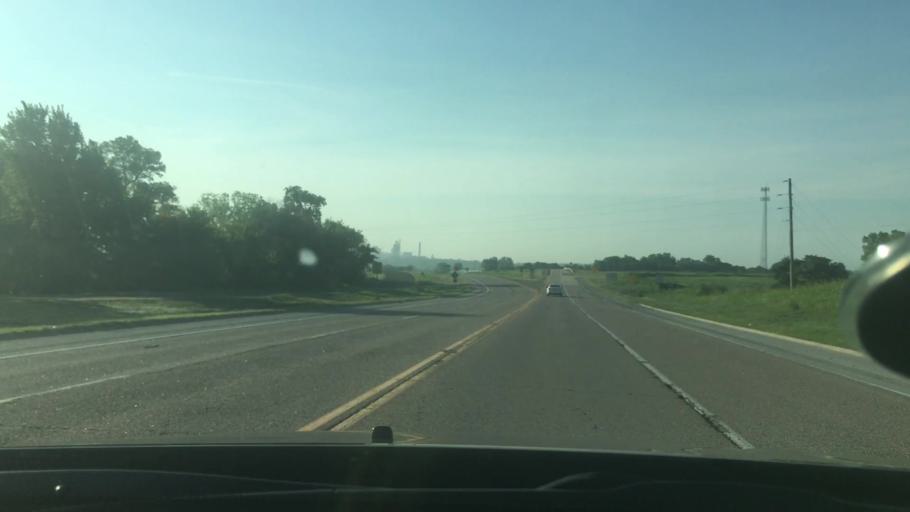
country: US
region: Oklahoma
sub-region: Pontotoc County
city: Ada
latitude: 34.7885
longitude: -96.7281
